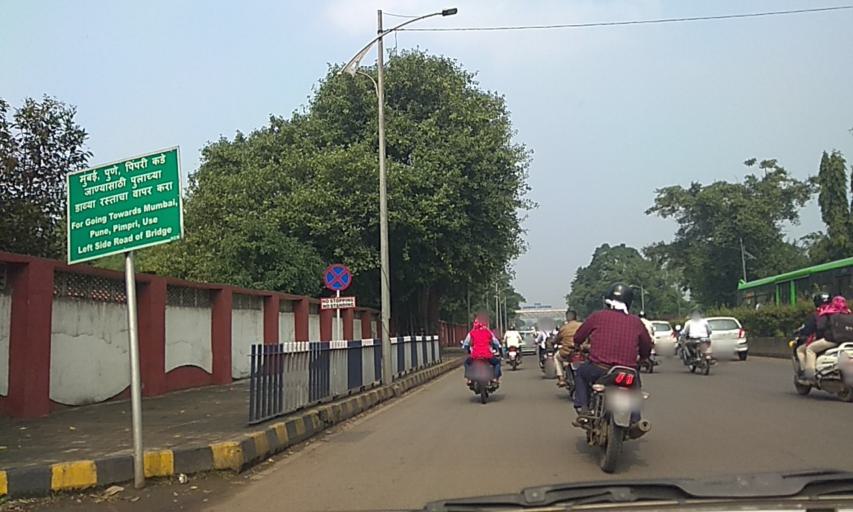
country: IN
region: Maharashtra
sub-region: Pune Division
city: Khadki
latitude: 18.5488
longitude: 73.8708
